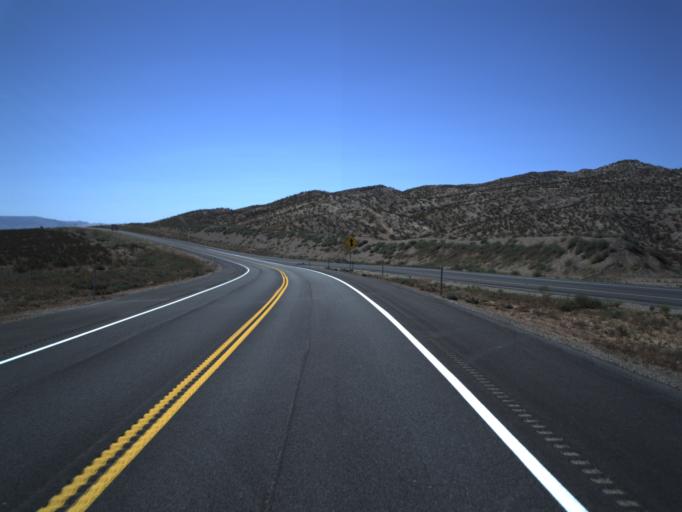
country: US
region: Utah
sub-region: Washington County
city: Washington
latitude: 37.1106
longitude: -113.4606
